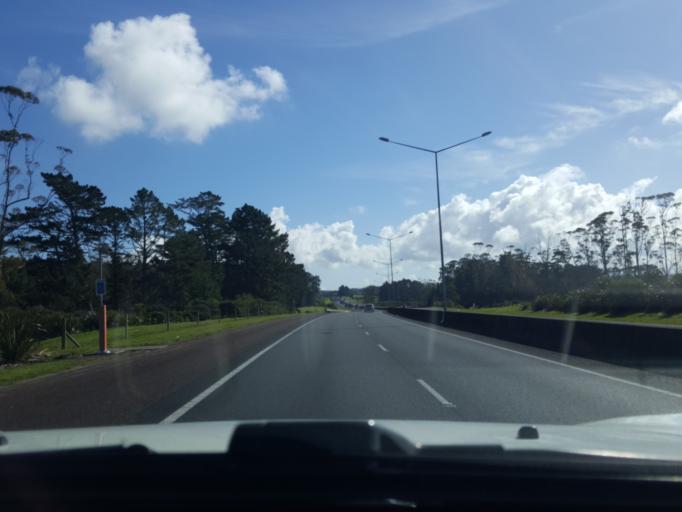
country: NZ
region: Auckland
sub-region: Auckland
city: Rosebank
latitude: -36.8049
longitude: 174.6051
